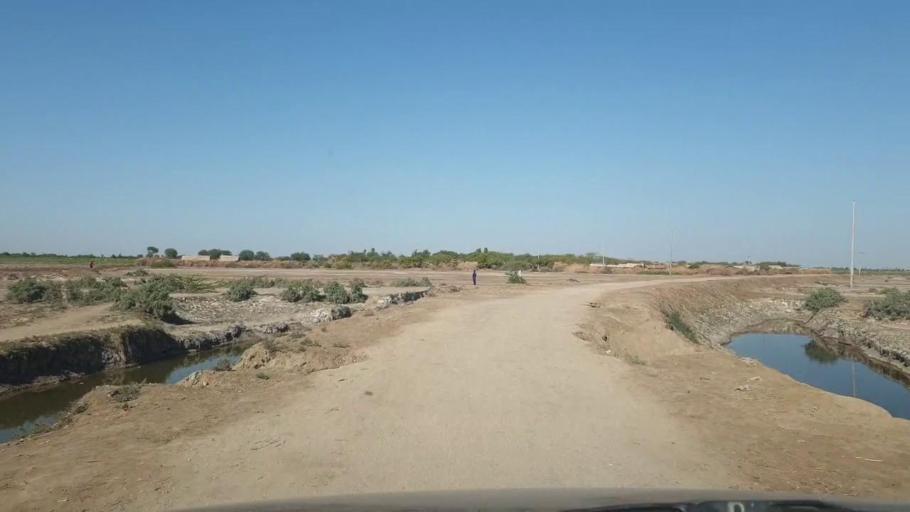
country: PK
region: Sindh
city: Dhoro Naro
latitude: 25.4131
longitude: 69.5817
